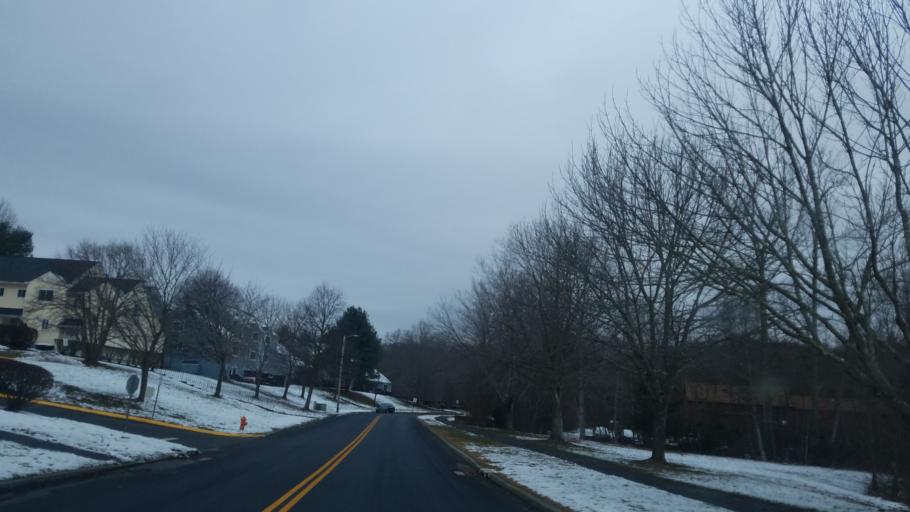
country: US
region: Connecticut
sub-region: New London County
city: Central Waterford
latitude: 41.3504
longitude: -72.1596
